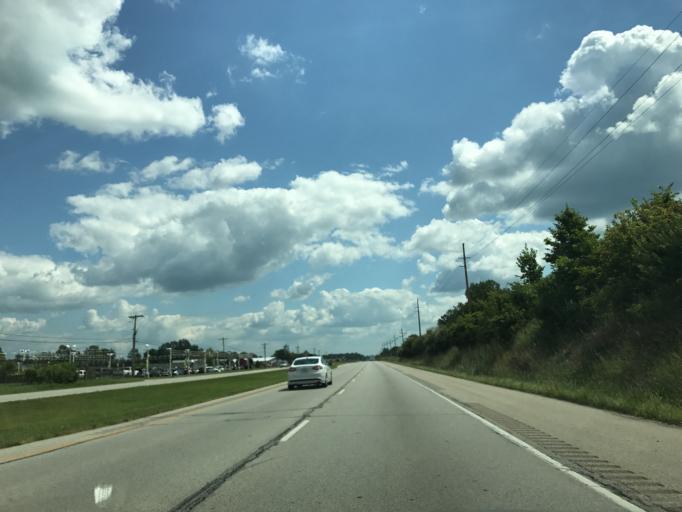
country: US
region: Indiana
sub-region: Kosciusko County
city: Winona Lake
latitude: 41.2229
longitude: -85.7875
